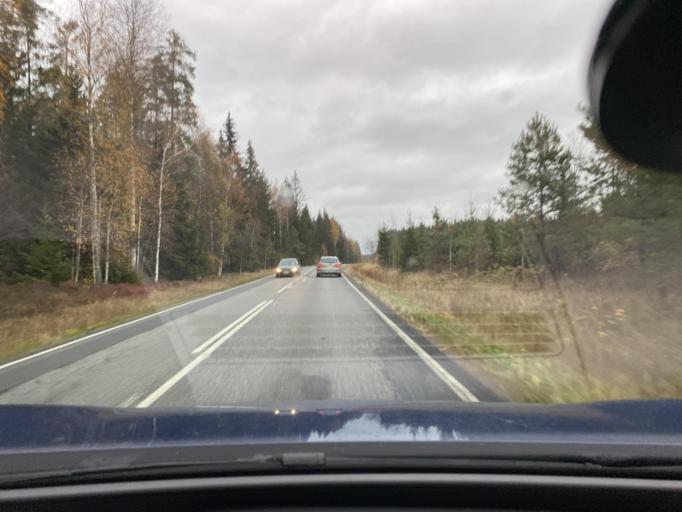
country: FI
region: Satakunta
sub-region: Pori
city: Huittinen
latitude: 61.1205
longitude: 22.5743
